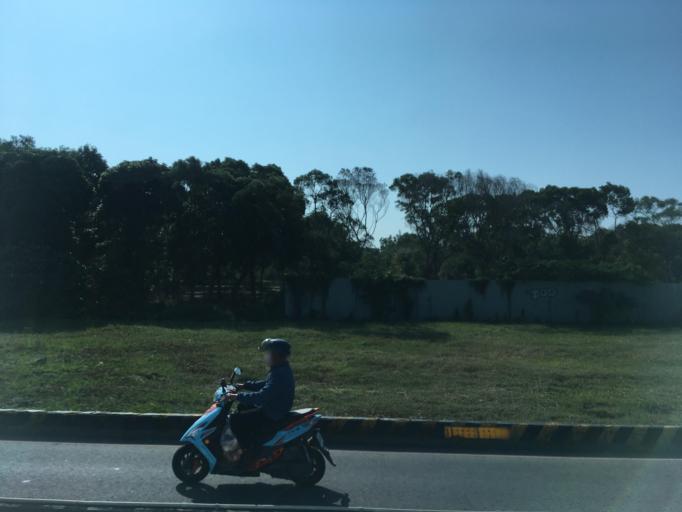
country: TW
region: Taiwan
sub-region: Chiayi
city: Jiayi Shi
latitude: 23.4951
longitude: 120.4460
